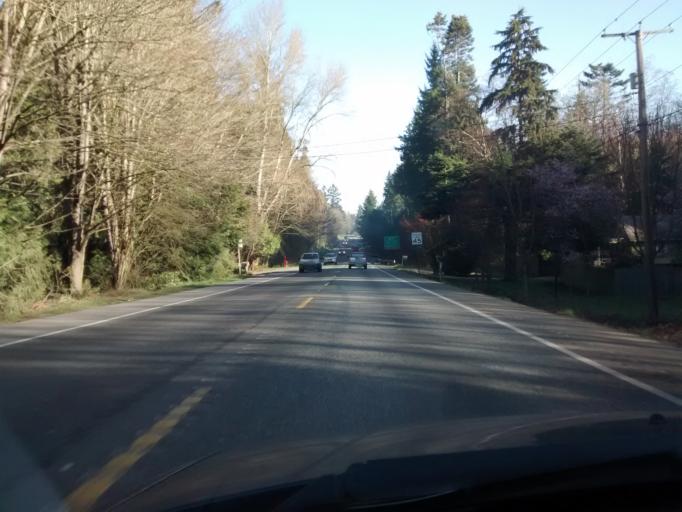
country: US
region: Washington
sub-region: Kitsap County
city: Lofall
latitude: 47.8446
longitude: -122.6153
